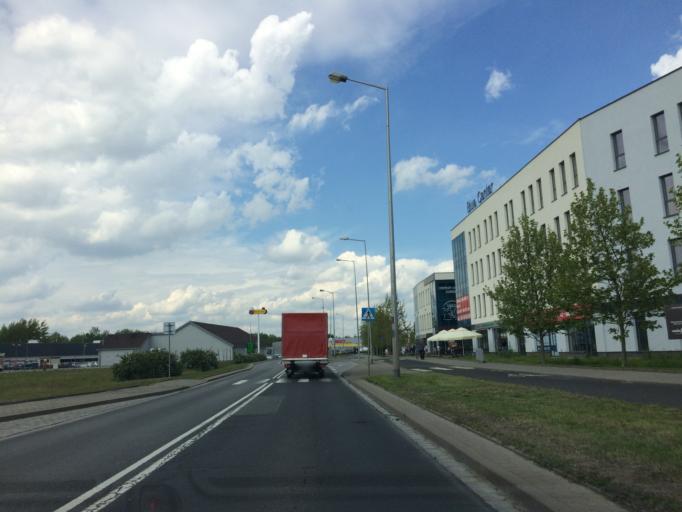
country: PL
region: Lower Silesian Voivodeship
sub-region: Powiat wroclawski
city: Smolec
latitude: 51.1546
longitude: 16.9241
